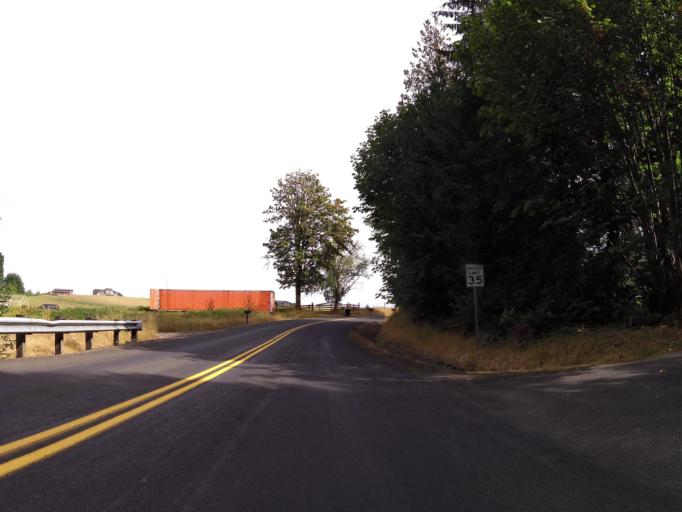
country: US
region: Washington
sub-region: Cowlitz County
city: Castle Rock
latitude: 46.3231
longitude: -122.9287
